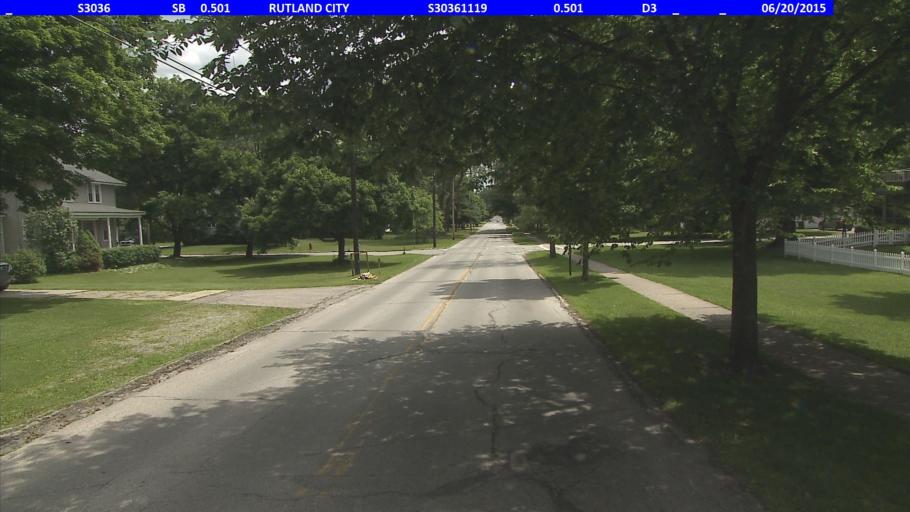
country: US
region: Vermont
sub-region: Rutland County
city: Rutland
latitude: 43.6155
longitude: -72.9769
